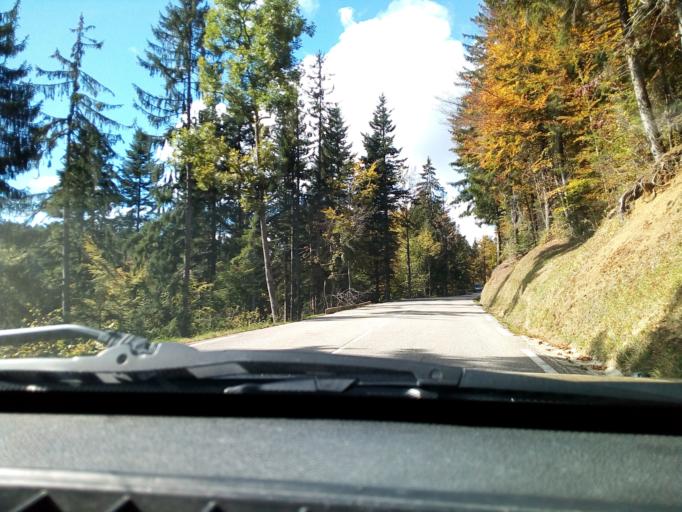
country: FR
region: Rhone-Alpes
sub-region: Departement de l'Isere
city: Le Sappey-en-Chartreuse
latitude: 45.2715
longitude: 5.7687
